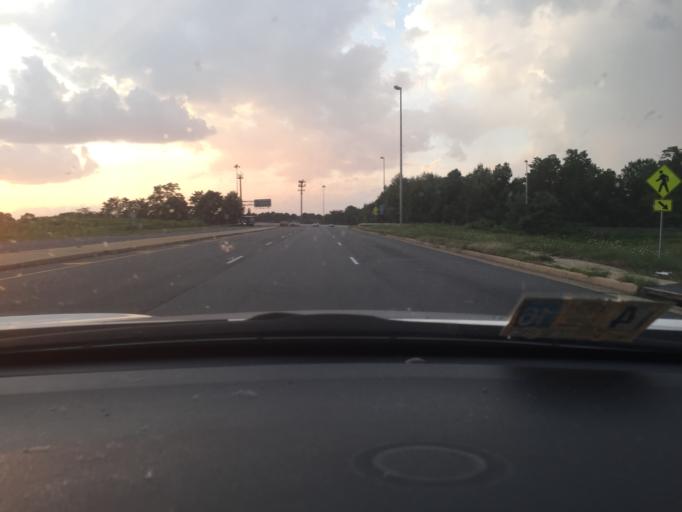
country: US
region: Virginia
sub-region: Fairfax County
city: Mantua
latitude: 38.8763
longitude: -77.2655
